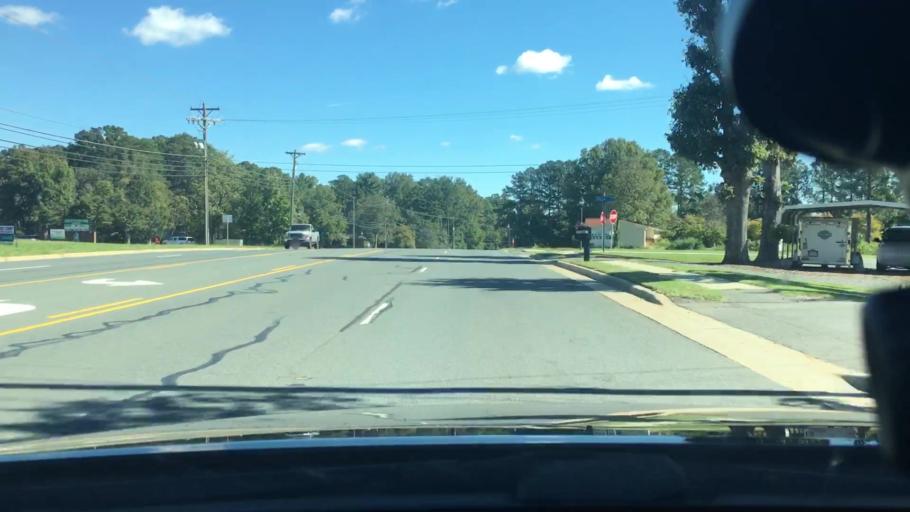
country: US
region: North Carolina
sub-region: Stanly County
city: Locust
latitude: 35.2617
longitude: -80.4190
